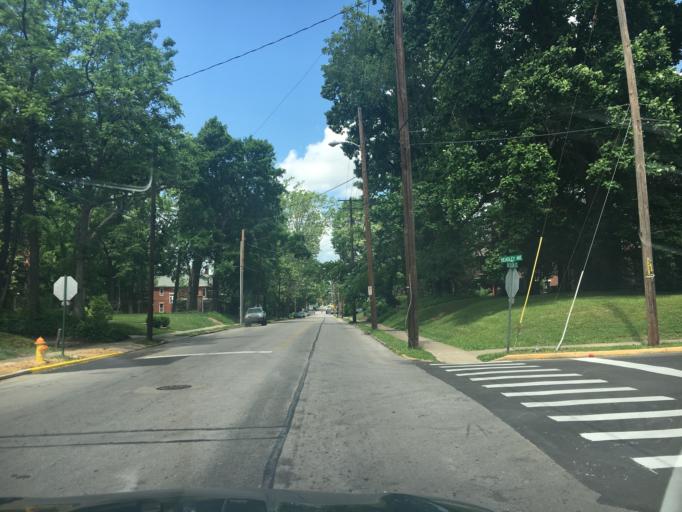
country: US
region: Kentucky
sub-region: Fayette County
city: Mount Vernon
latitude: 38.0576
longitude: -84.4903
